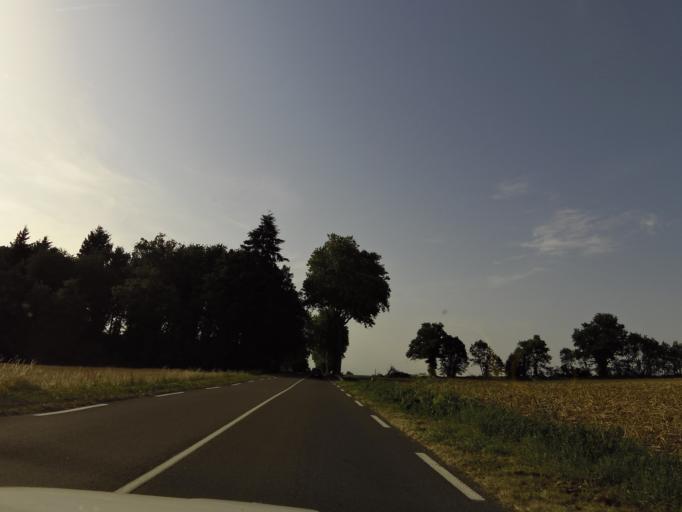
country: FR
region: Rhone-Alpes
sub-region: Departement de l'Ain
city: Meximieux
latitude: 45.9284
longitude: 5.1856
